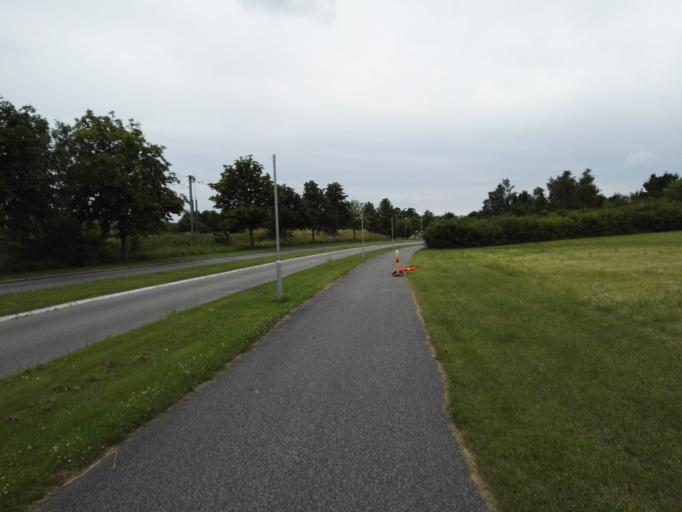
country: DK
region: Capital Region
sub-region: Egedal Kommune
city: Vekso
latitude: 55.7504
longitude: 12.2457
